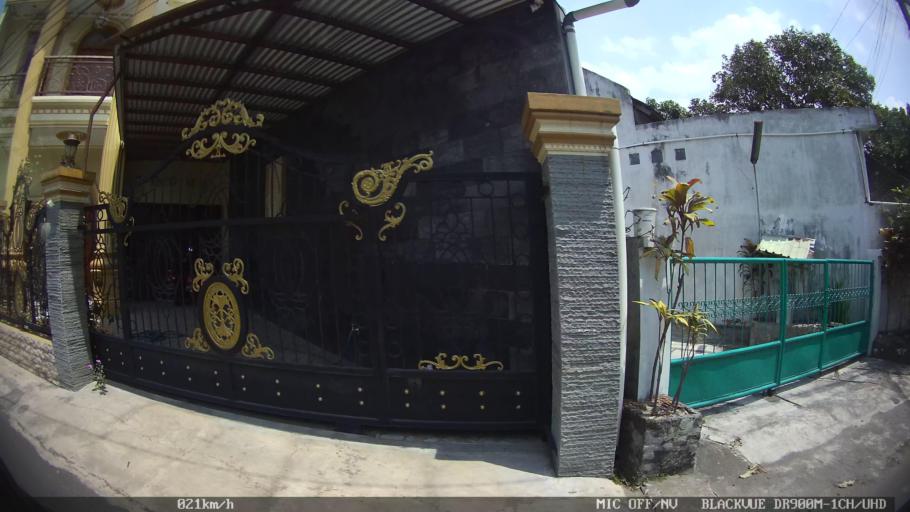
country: ID
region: Daerah Istimewa Yogyakarta
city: Yogyakarta
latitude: -7.8238
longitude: 110.4063
